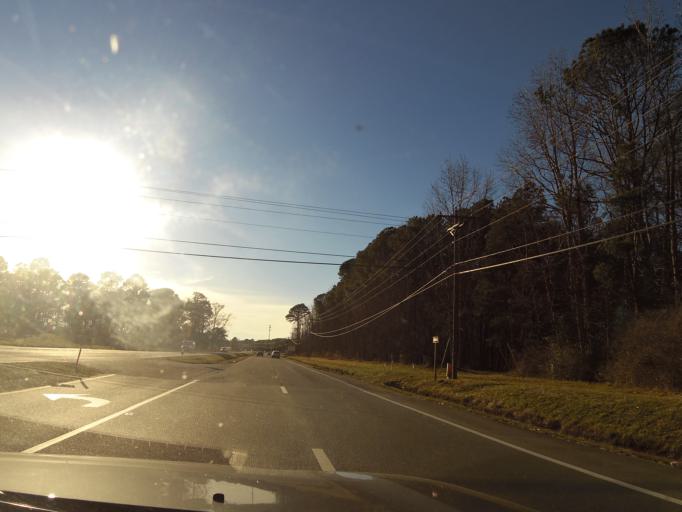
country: US
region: Virginia
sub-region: City of Suffolk
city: South Suffolk
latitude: 36.7014
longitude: -76.7005
